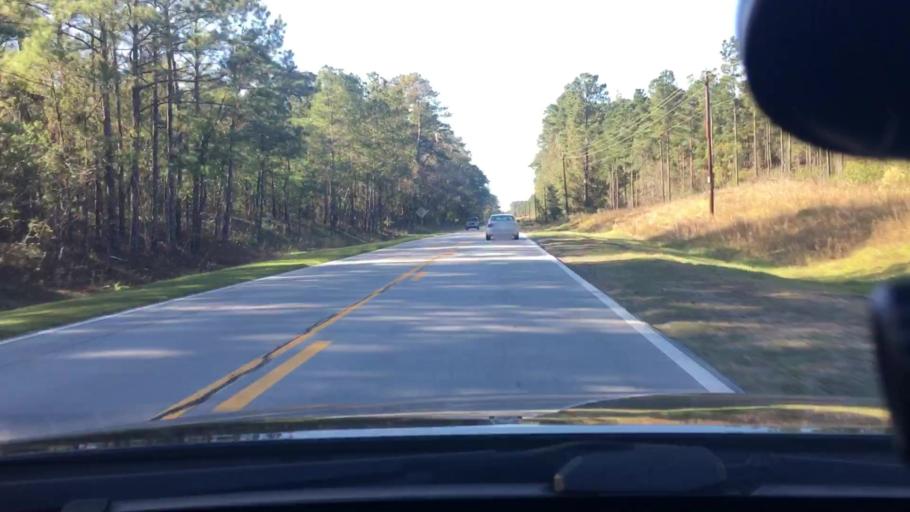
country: US
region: North Carolina
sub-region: Craven County
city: Vanceboro
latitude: 35.2197
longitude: -77.1236
